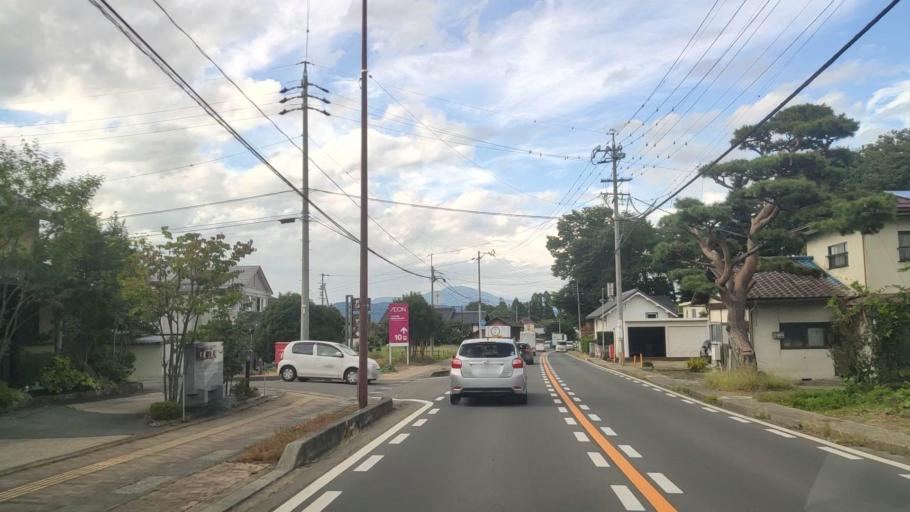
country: JP
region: Nagano
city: Suzaka
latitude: 36.6914
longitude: 138.3152
